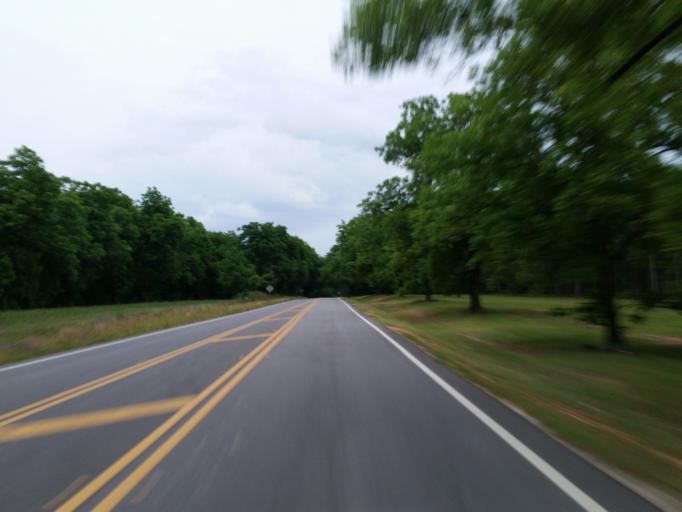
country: US
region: Georgia
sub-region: Crisp County
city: Cordele
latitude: 31.8672
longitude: -83.7485
